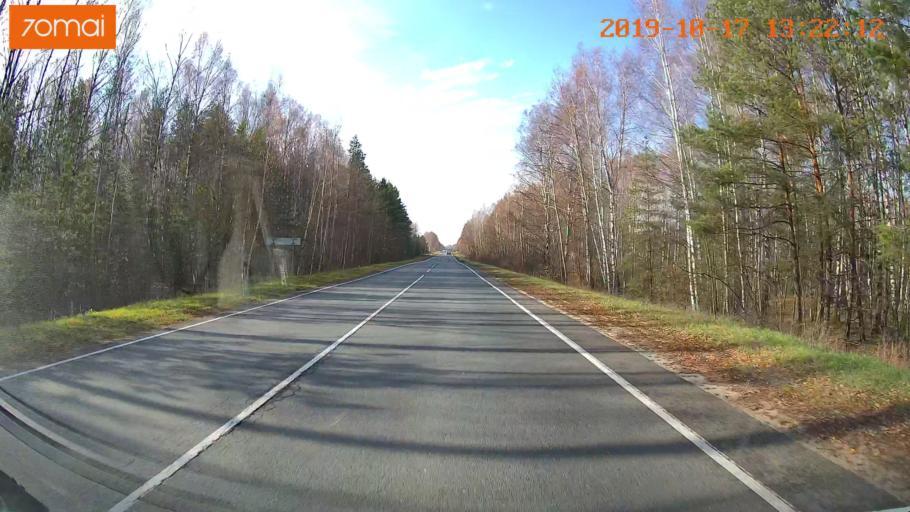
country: RU
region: Rjazan
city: Gus'-Zheleznyy
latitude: 55.0852
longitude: 41.0091
